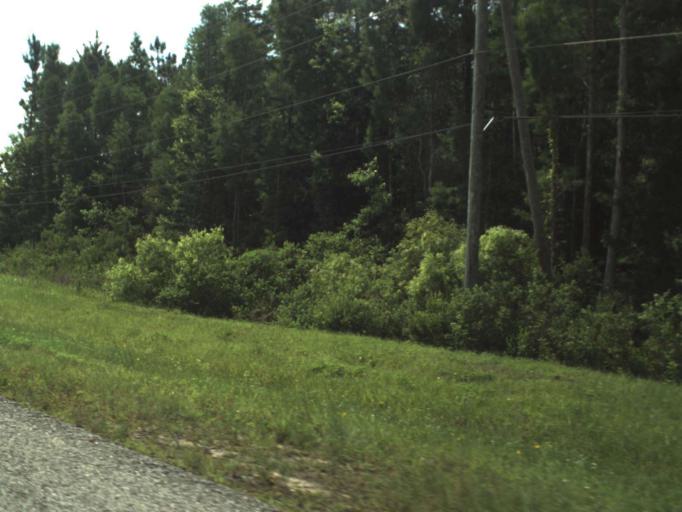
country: US
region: Florida
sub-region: Volusia County
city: Samsula-Spruce Creek
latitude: 29.0248
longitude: -81.1257
